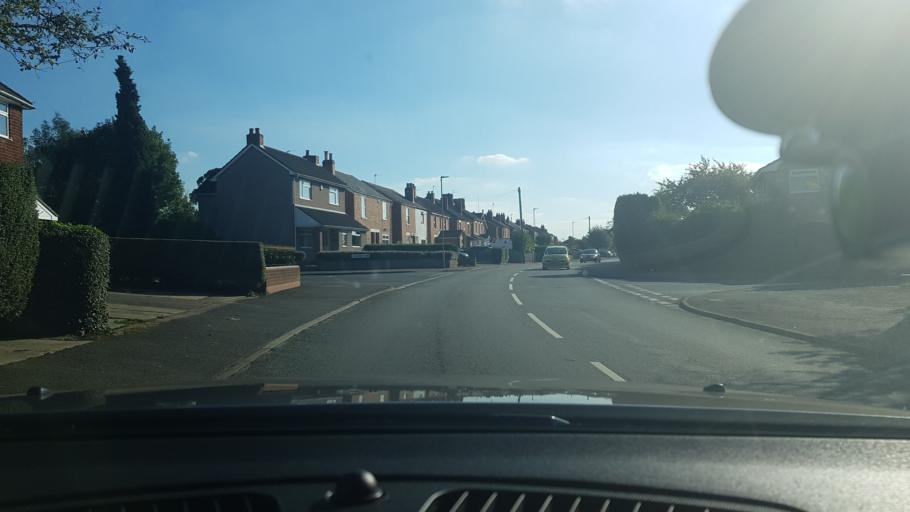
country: GB
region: England
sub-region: Gloucestershire
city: Gloucester
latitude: 51.8341
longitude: -2.2558
